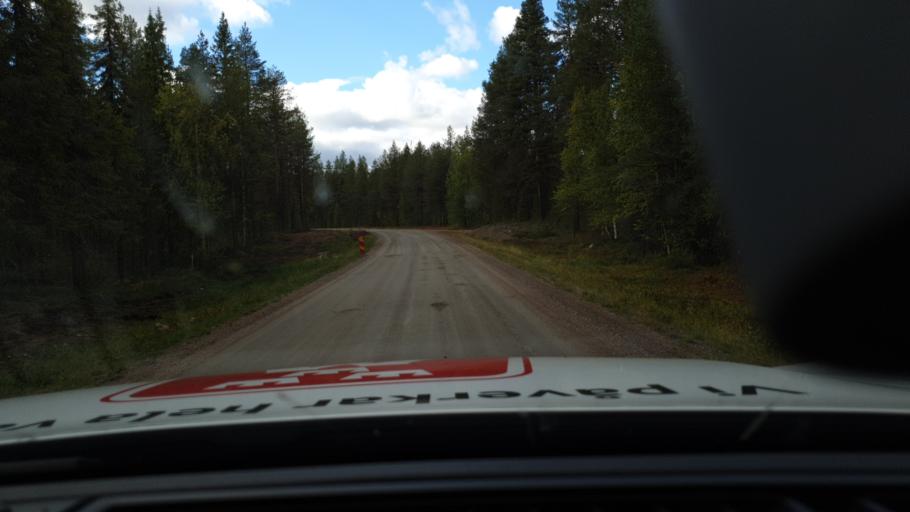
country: FI
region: Lapland
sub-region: Tunturi-Lappi
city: Kolari
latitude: 67.4580
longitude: 23.5456
